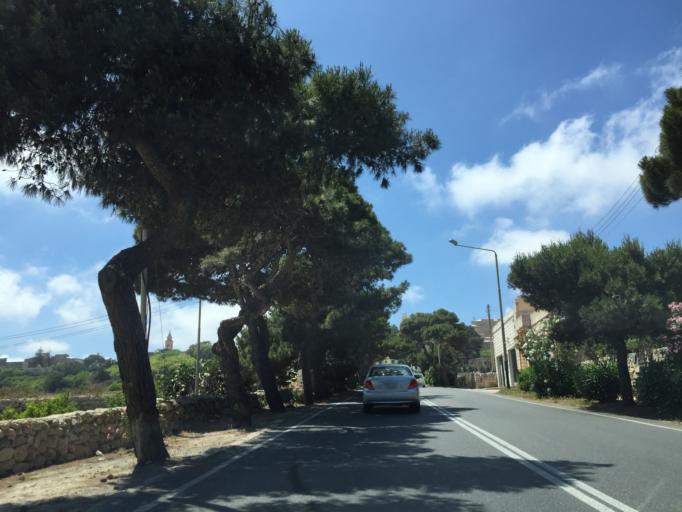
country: MT
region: L-Imdina
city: Imdina
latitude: 35.8830
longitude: 14.4075
